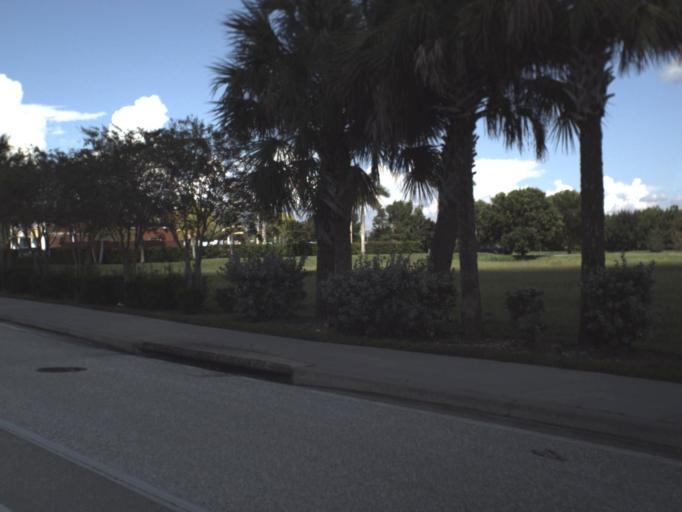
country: US
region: Florida
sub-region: Lee County
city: Palmona Park
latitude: 26.6990
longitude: -81.9418
